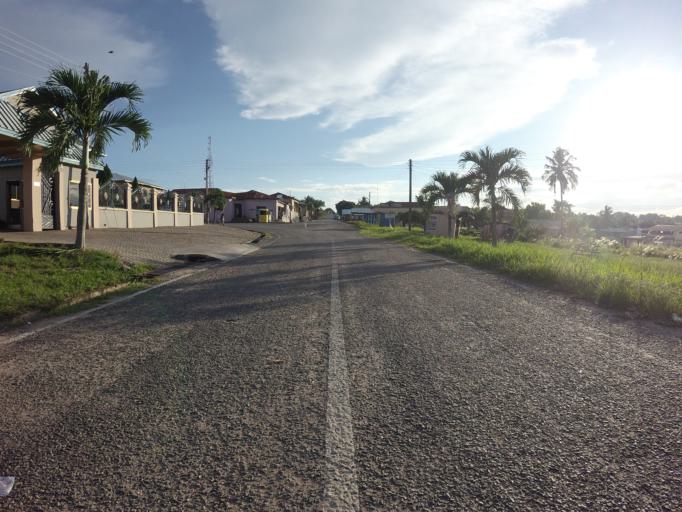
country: GH
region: Ashanti
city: Tafo
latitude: 6.9419
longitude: -1.6748
